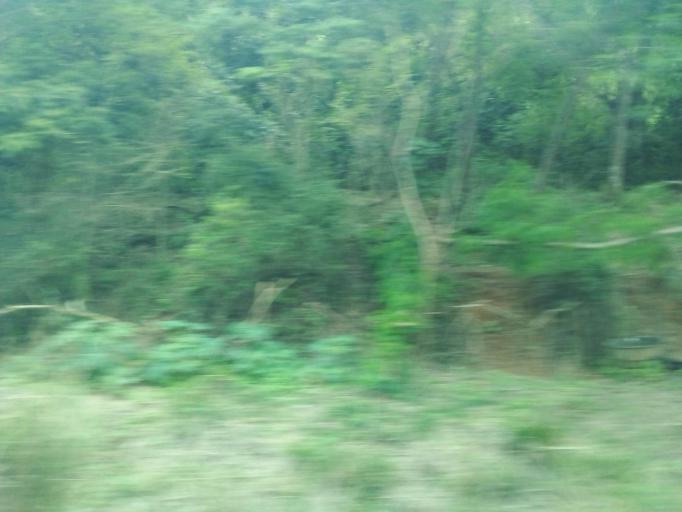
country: BR
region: Minas Gerais
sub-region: Ipaba
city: Ipaba
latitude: -19.4621
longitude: -42.4506
